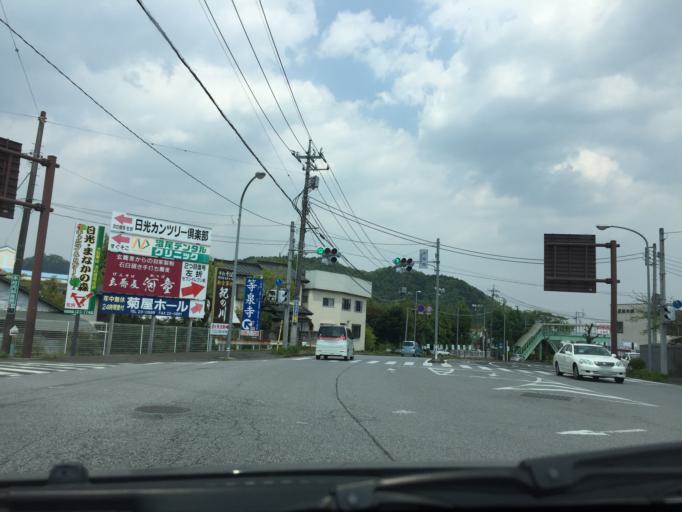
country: JP
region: Tochigi
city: Imaichi
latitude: 36.7328
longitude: 139.6884
